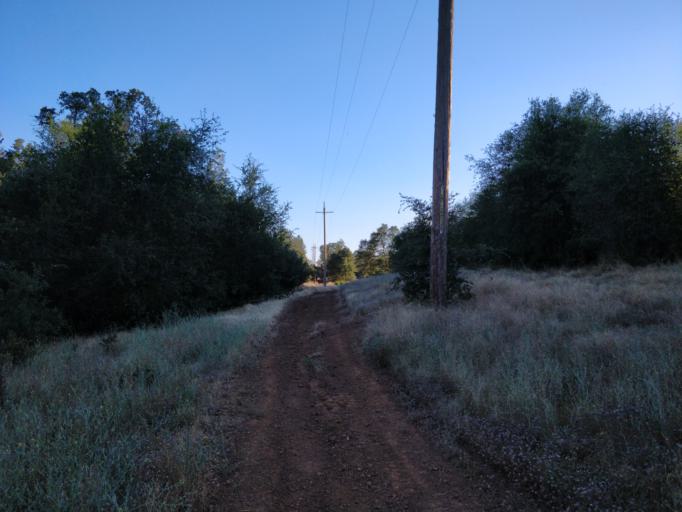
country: US
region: California
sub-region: Shasta County
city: Shasta Lake
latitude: 40.6668
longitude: -122.3665
